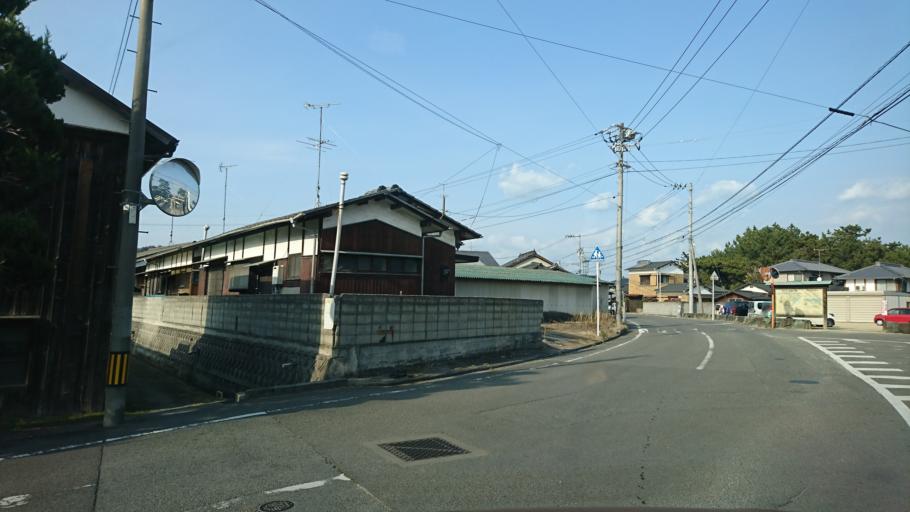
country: JP
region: Ehime
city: Saijo
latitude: 34.0184
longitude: 133.0413
